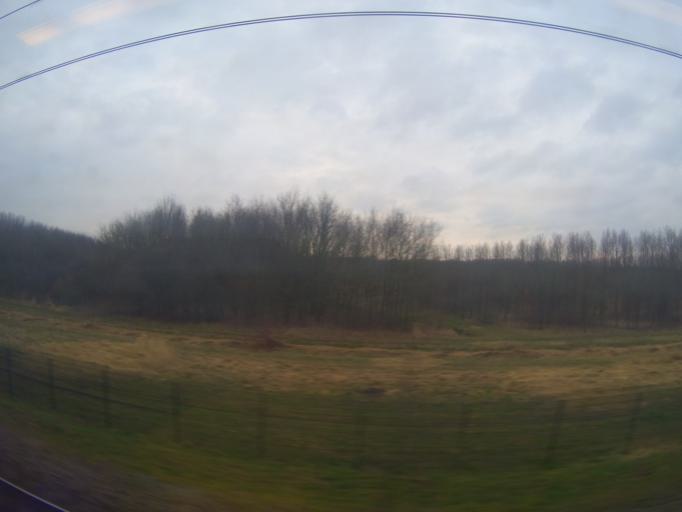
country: NL
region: South Holland
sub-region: Gemeente Pijnacker-Nootdorp
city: Pijnacker
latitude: 52.0497
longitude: 4.4489
